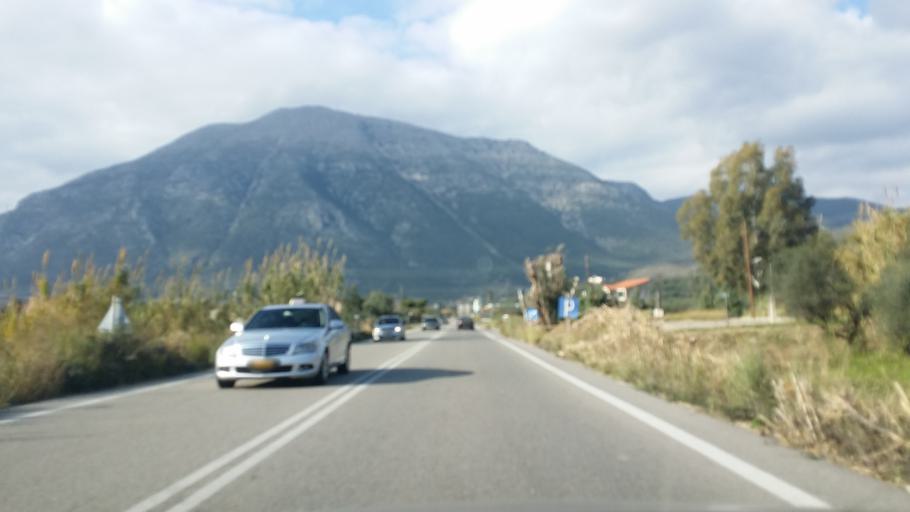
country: GR
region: West Greece
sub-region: Nomos Aitolias kai Akarnanias
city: Antirrio
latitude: 38.3457
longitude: 21.7227
